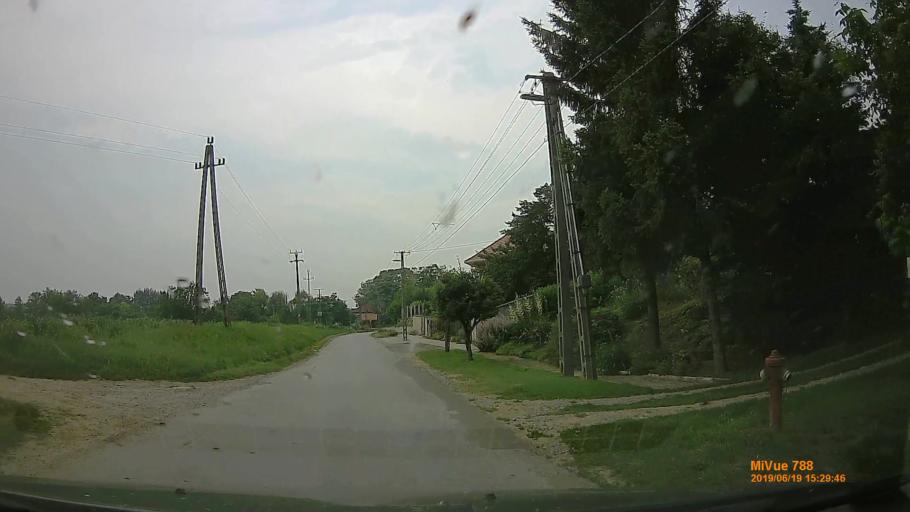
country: HU
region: Baranya
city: Szigetvar
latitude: 46.0676
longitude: 17.8470
